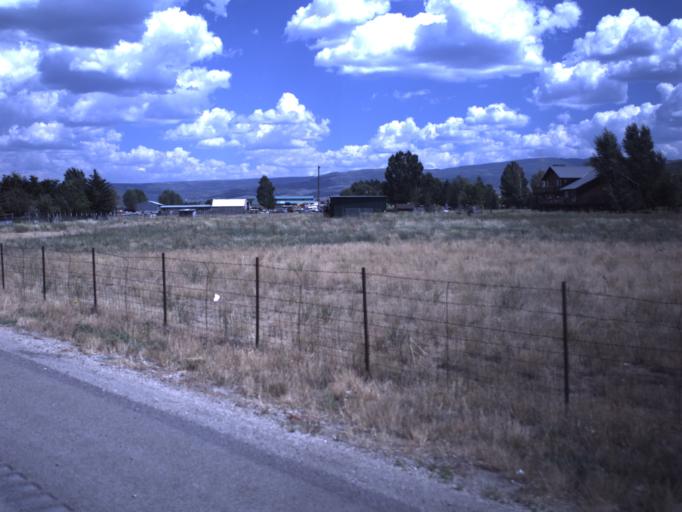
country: US
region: Utah
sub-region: Wasatch County
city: Heber
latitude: 40.4715
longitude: -111.4467
